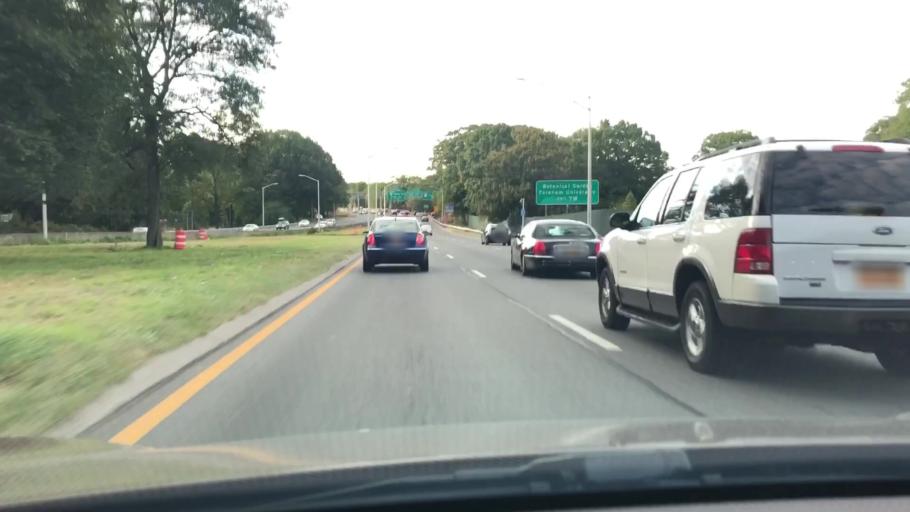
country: US
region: New York
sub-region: Bronx
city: The Bronx
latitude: 40.8609
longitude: -73.8723
